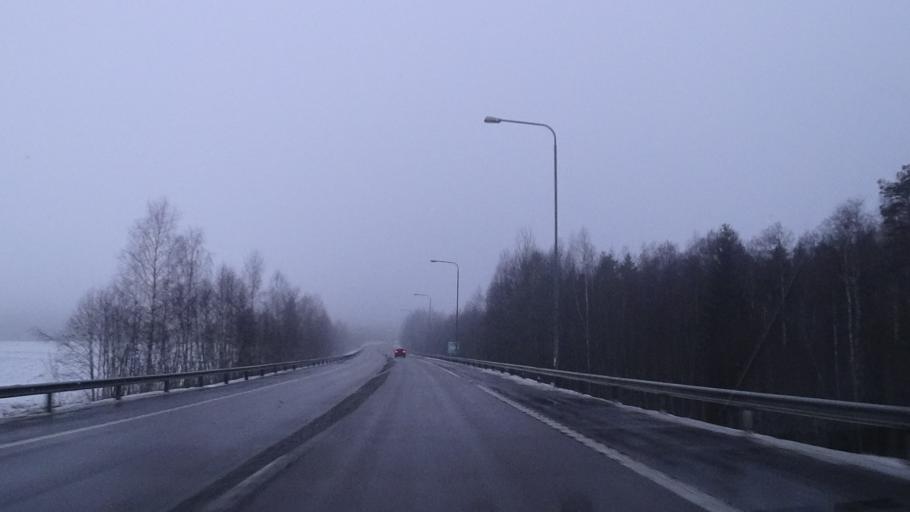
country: FI
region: Paijanne Tavastia
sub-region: Lahti
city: Hollola
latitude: 60.9838
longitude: 25.4436
